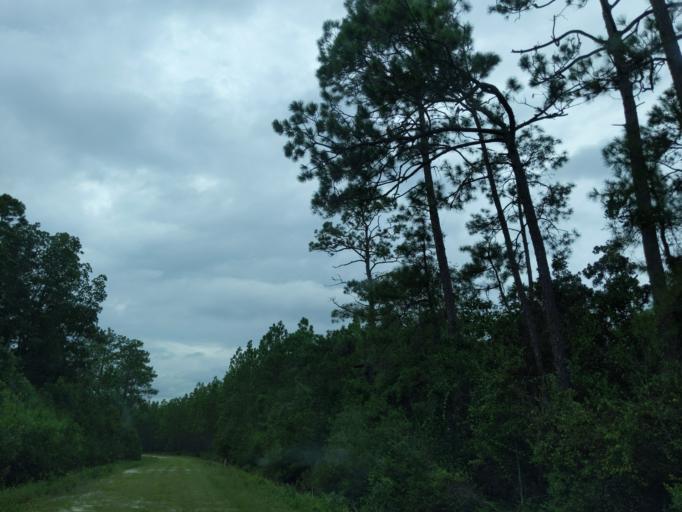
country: US
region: Florida
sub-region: Gadsden County
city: Midway
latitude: 30.3590
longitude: -84.4962
